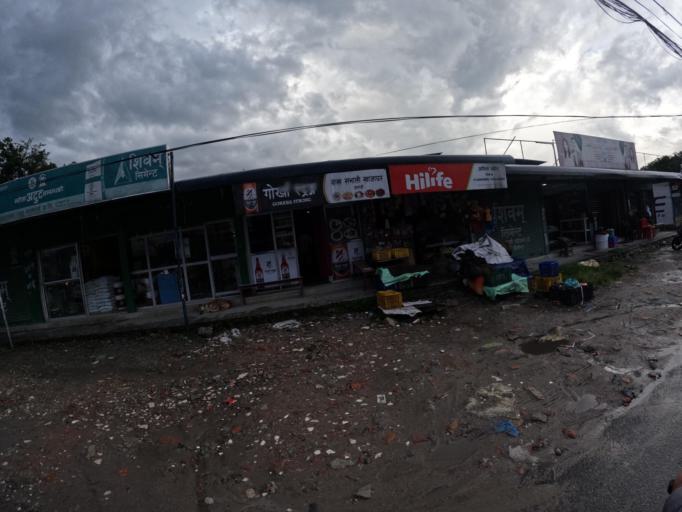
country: NP
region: Central Region
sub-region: Bagmati Zone
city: Kathmandu
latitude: 27.7559
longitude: 85.3278
